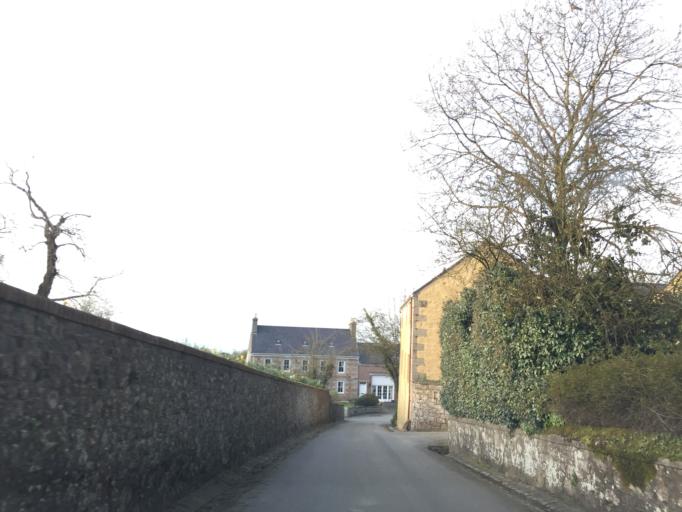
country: JE
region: St Helier
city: Saint Helier
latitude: 49.2305
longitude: -2.0601
